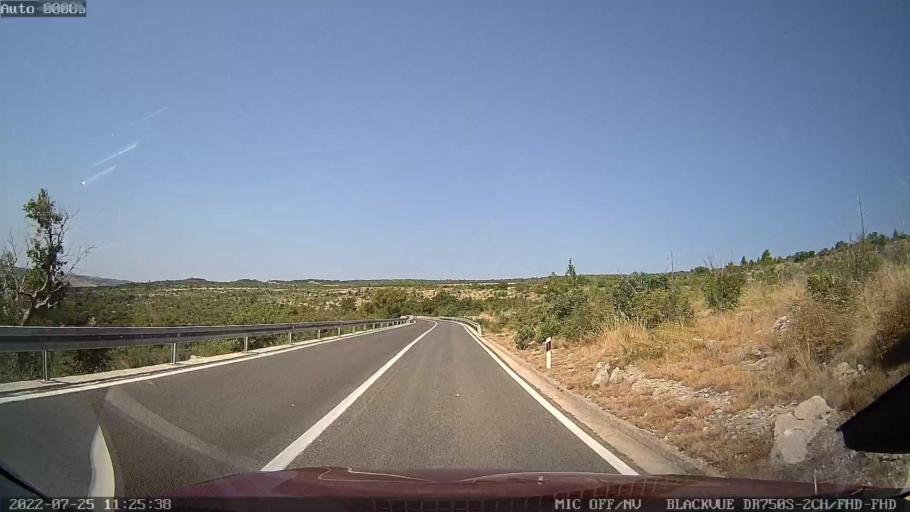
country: HR
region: Zadarska
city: Posedarje
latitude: 44.2224
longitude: 15.5185
